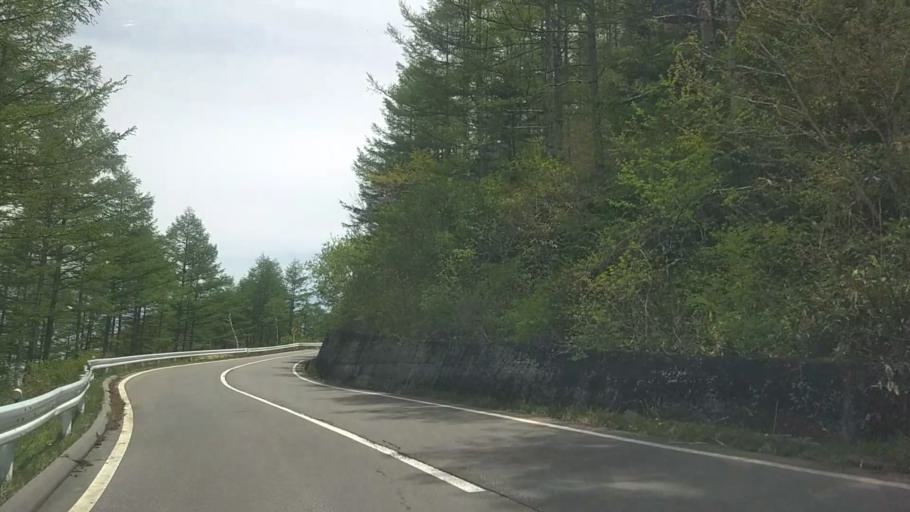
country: JP
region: Nagano
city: Saku
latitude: 36.0908
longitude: 138.3874
